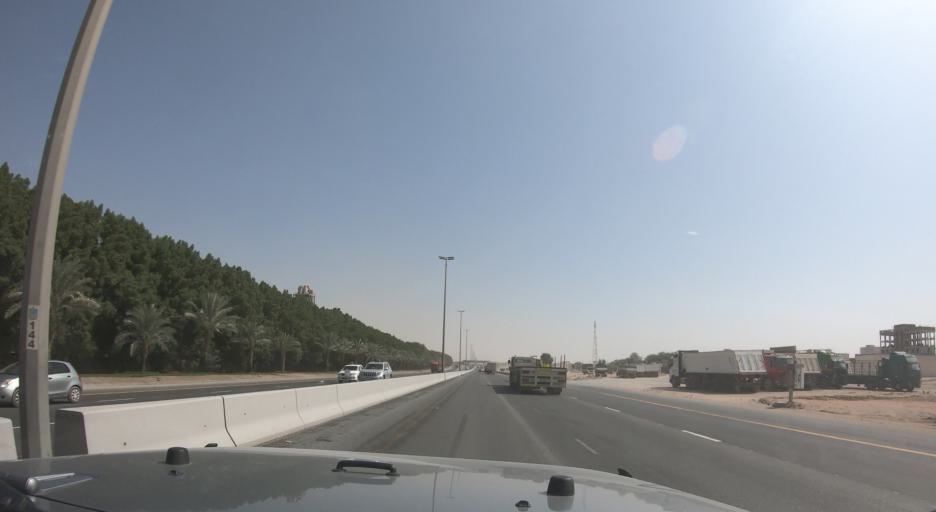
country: AE
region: Ash Shariqah
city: Sharjah
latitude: 25.2951
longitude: 55.6118
